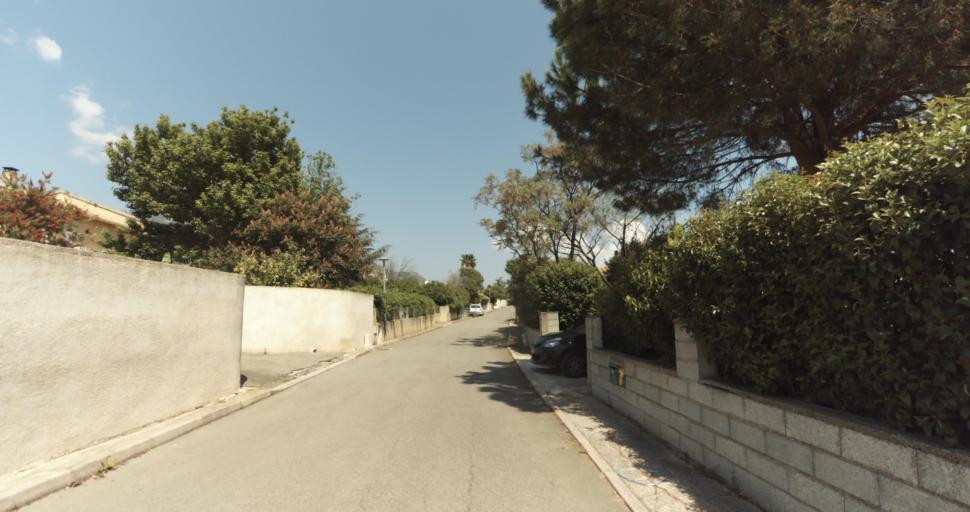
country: FR
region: Corsica
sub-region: Departement de la Haute-Corse
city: Biguglia
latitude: 42.6042
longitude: 9.4318
